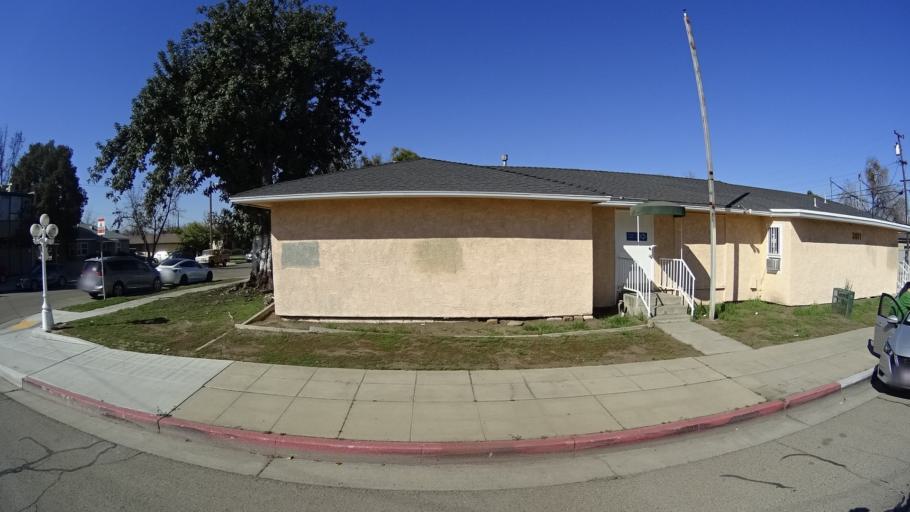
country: US
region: California
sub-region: Fresno County
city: Fresno
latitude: 36.7743
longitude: -119.7816
